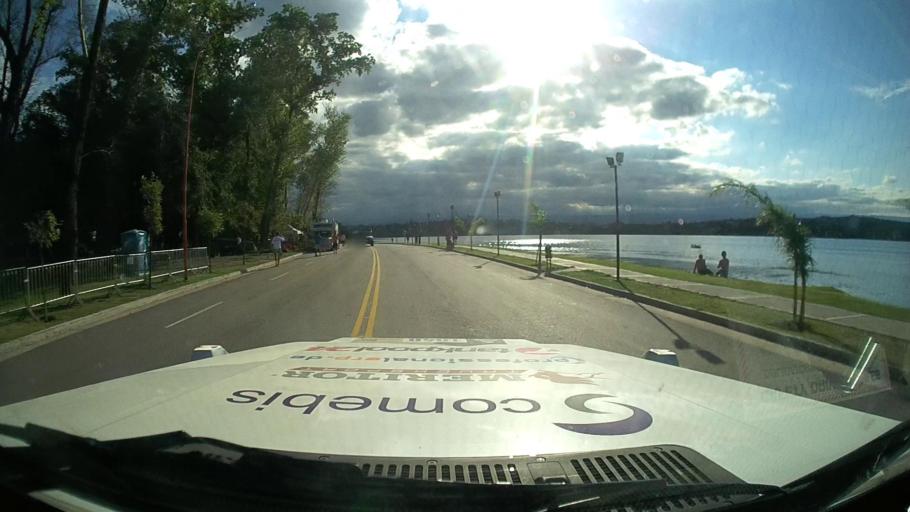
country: AR
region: Cordoba
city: Villa Carlos Paz
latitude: -31.3987
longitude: -64.4809
